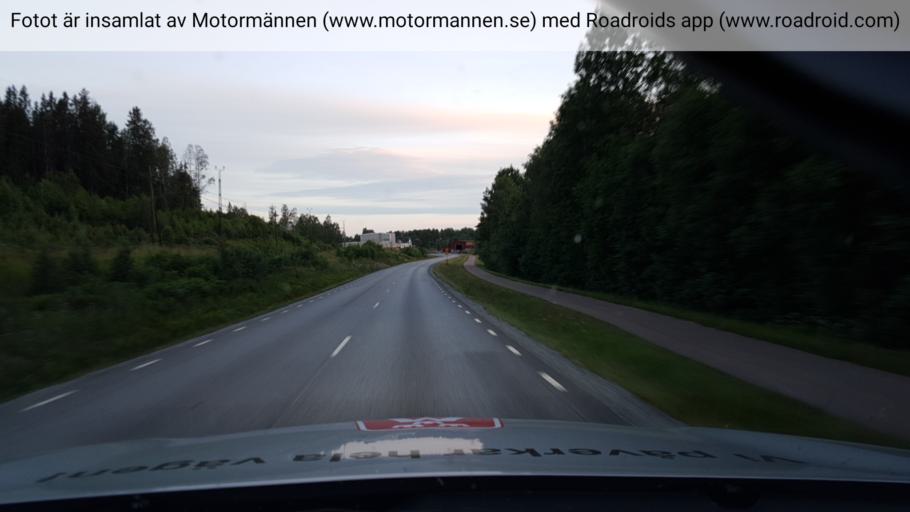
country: SE
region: Vaestmanland
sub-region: Skinnskattebergs Kommun
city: Skinnskatteberg
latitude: 59.8377
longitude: 15.7030
